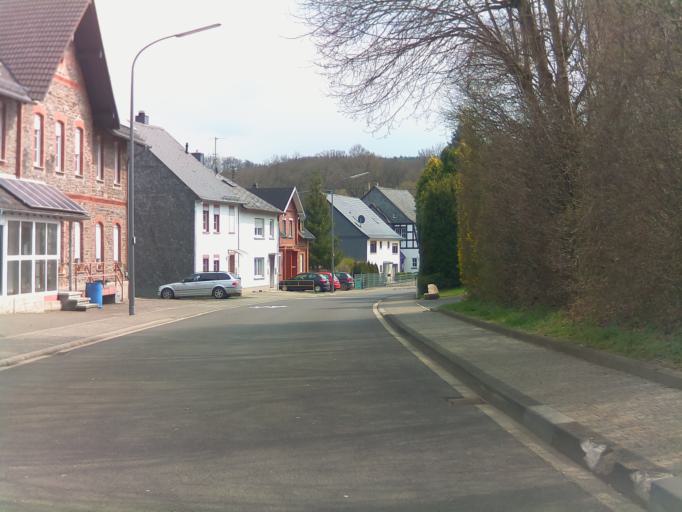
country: DE
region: Rheinland-Pfalz
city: Rhaunen
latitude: 49.8626
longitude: 7.3496
